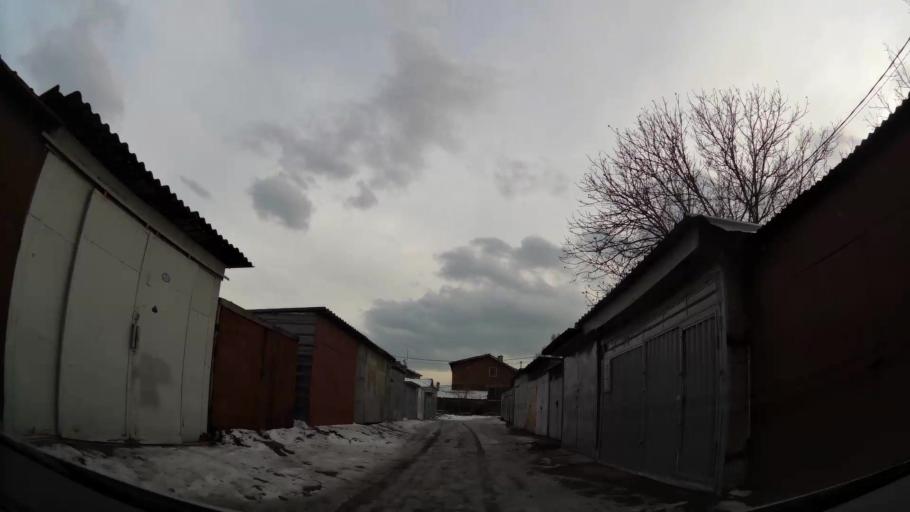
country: BG
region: Sofia-Capital
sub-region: Stolichna Obshtina
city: Sofia
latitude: 42.7269
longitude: 23.3456
